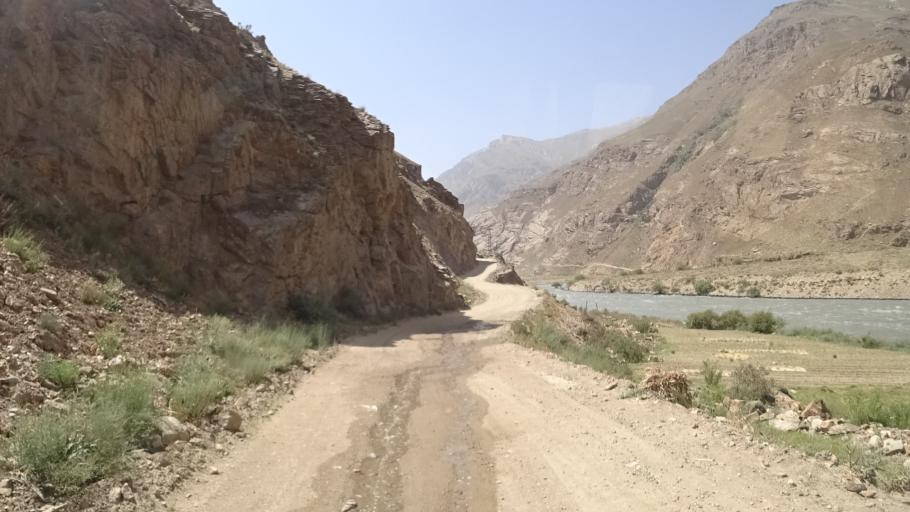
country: TJ
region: Gorno-Badakhshan
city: Khorugh
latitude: 37.1478
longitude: 71.4498
